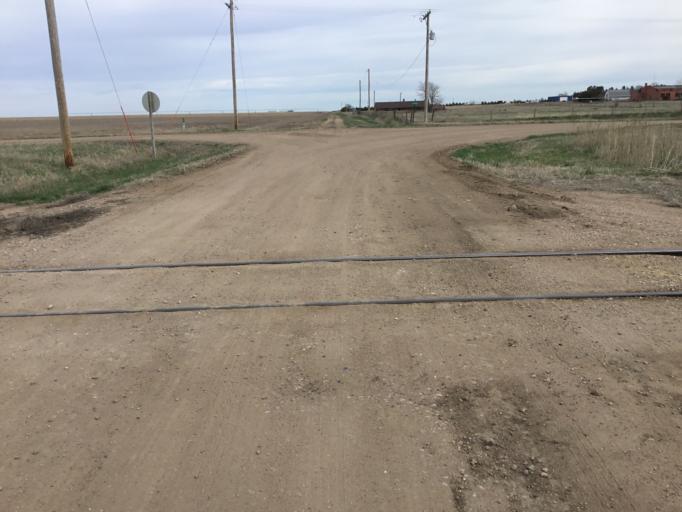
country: US
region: Kansas
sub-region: Sherman County
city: Goodland
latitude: 39.3385
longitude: -101.8932
